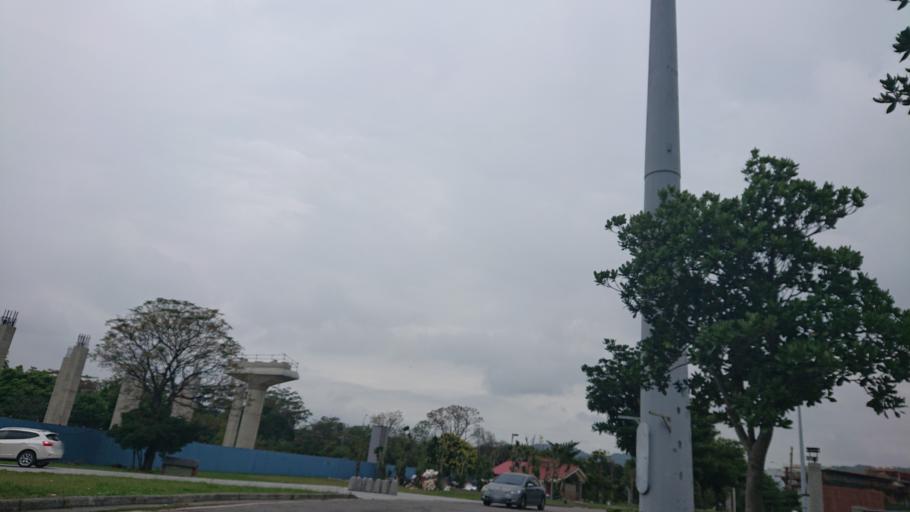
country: TW
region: Taiwan
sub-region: Taoyuan
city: Taoyuan
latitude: 24.9393
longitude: 121.3629
